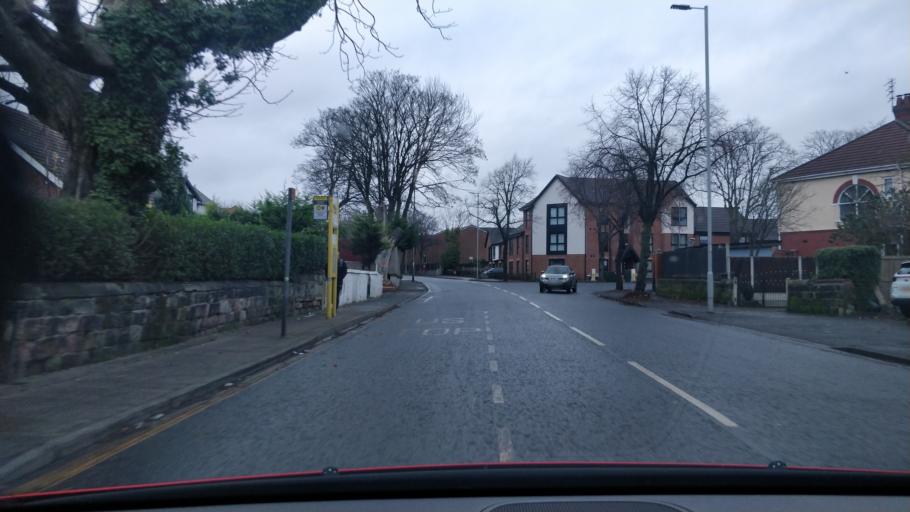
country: GB
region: England
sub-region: Sefton
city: Litherland
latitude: 53.4722
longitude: -2.9987
